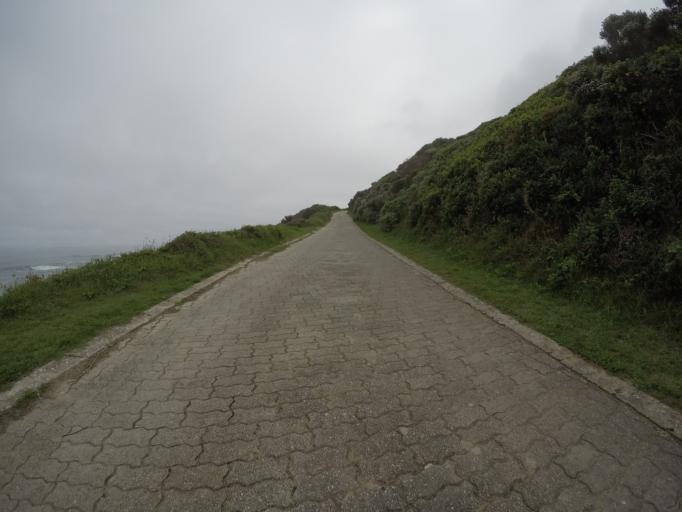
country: ZA
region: Eastern Cape
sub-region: Cacadu District Municipality
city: Kareedouw
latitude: -34.0697
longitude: 24.2124
